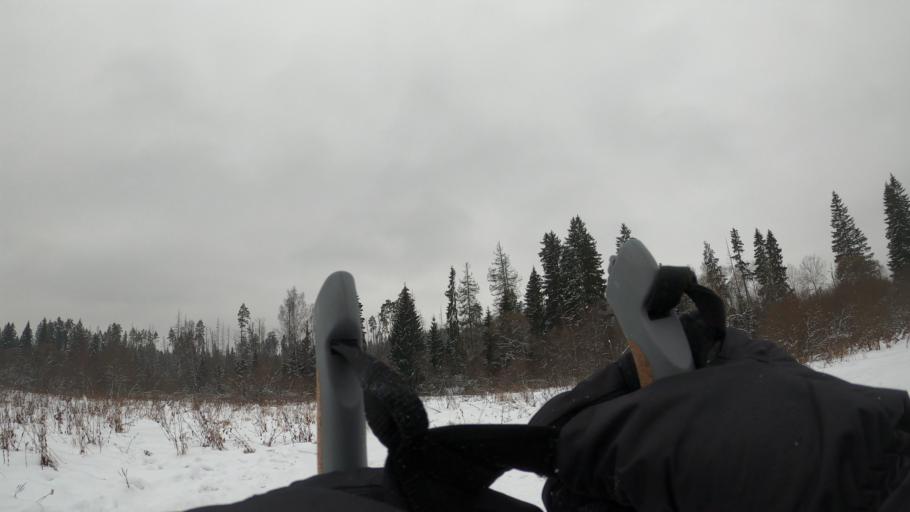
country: RU
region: Moskovskaya
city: Firsanovka
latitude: 55.9430
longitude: 37.2214
